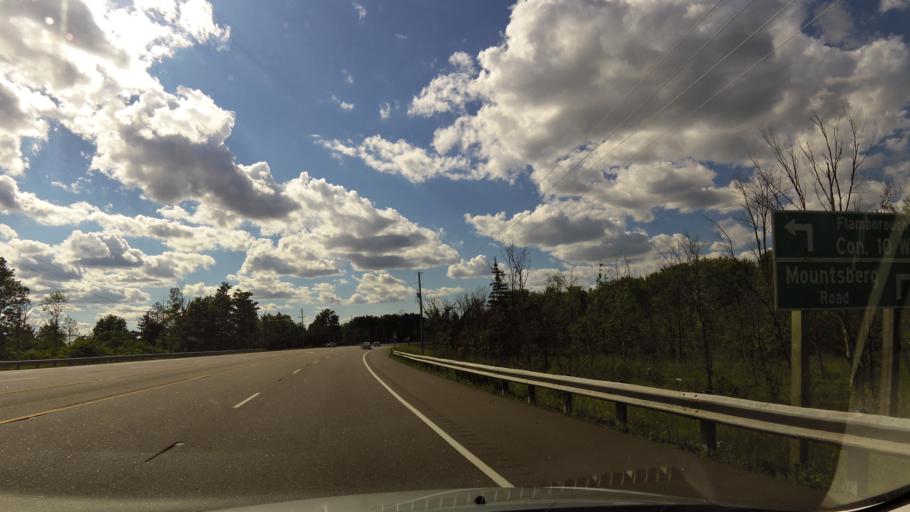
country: CA
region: Ontario
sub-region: Halton
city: Milton
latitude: 43.4105
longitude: -80.0539
